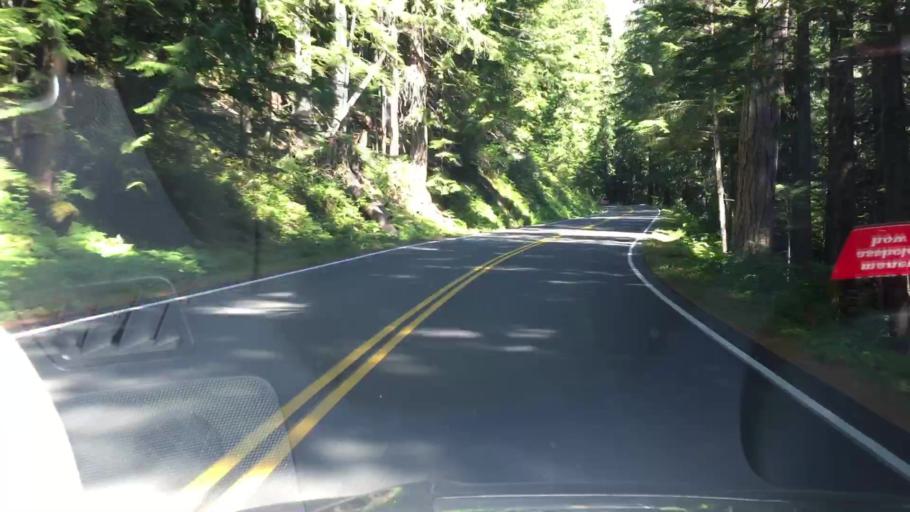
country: US
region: Washington
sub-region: Pierce County
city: Eatonville
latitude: 46.7350
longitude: -121.8687
